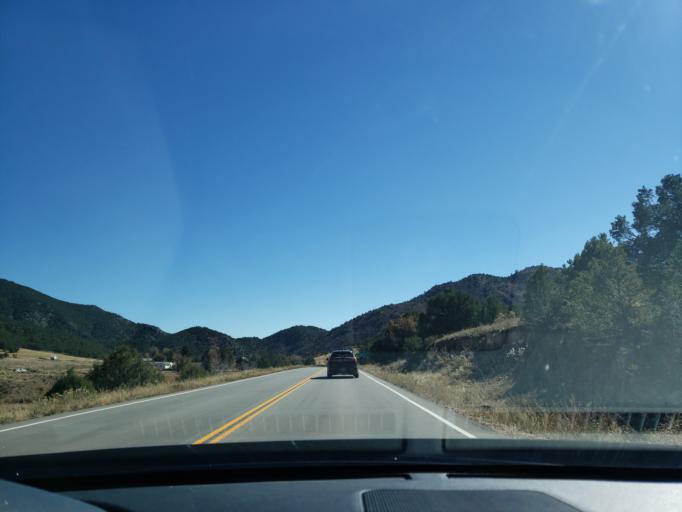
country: US
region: Colorado
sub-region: Fremont County
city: Canon City
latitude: 38.5871
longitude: -105.4207
